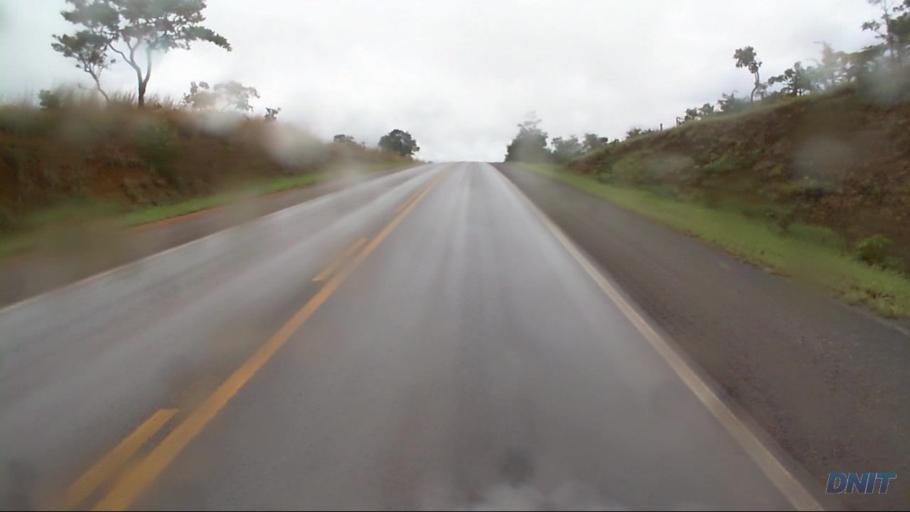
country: BR
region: Goias
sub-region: Padre Bernardo
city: Padre Bernardo
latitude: -15.2001
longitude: -48.4519
